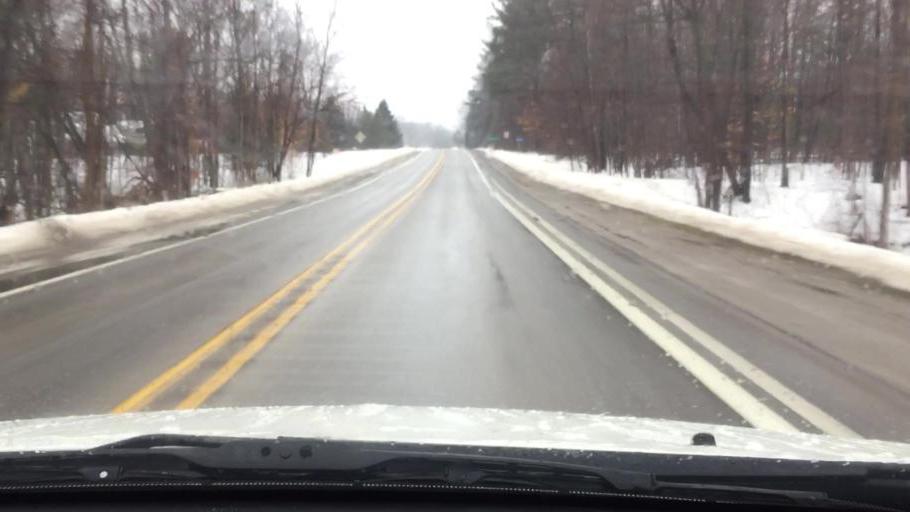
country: US
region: Michigan
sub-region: Charlevoix County
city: East Jordan
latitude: 45.1794
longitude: -85.1641
